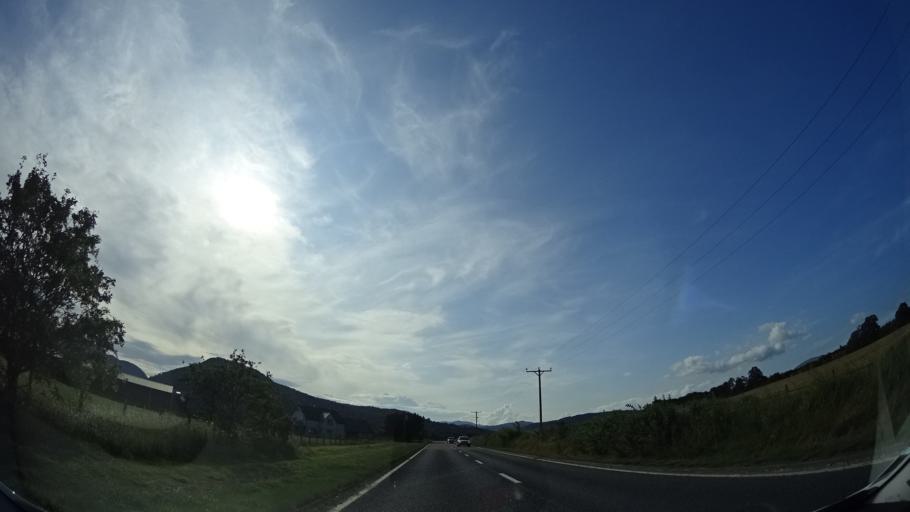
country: GB
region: Scotland
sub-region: Highland
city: Muir of Ord
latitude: 57.5621
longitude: -4.5682
